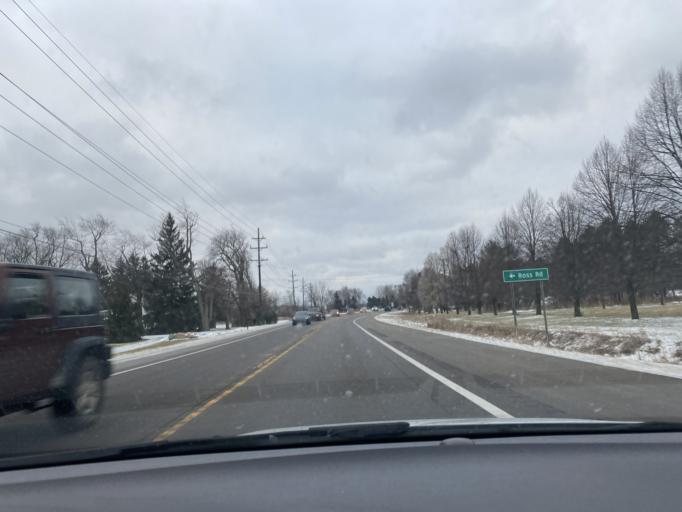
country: US
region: Michigan
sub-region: Lapeer County
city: Imlay City
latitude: 42.9804
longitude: -83.0601
